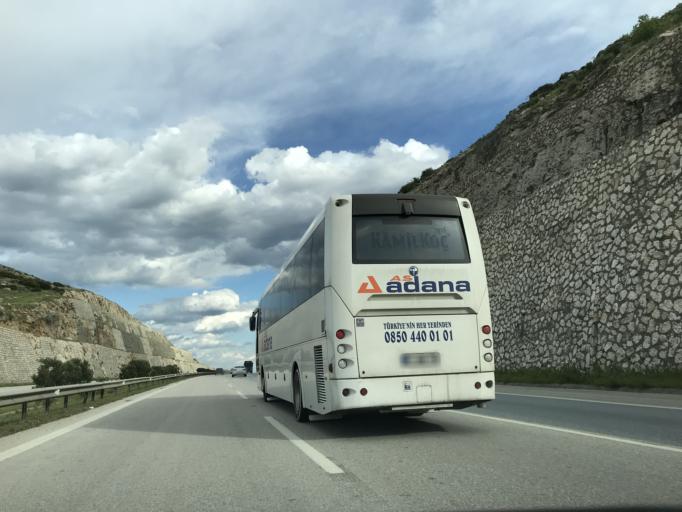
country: TR
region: Adana
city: Ceyhan
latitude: 36.9991
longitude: 35.7325
